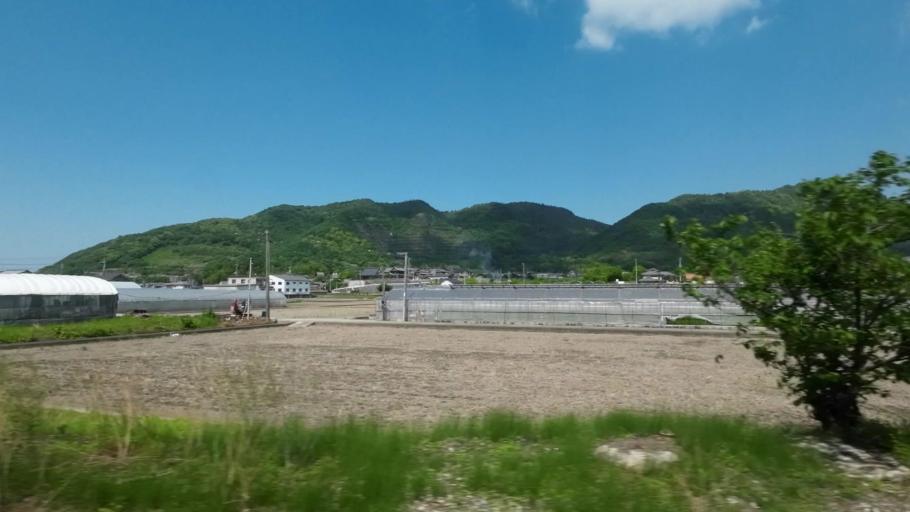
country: JP
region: Kagawa
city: Kan'onjicho
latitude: 34.1463
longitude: 133.6863
